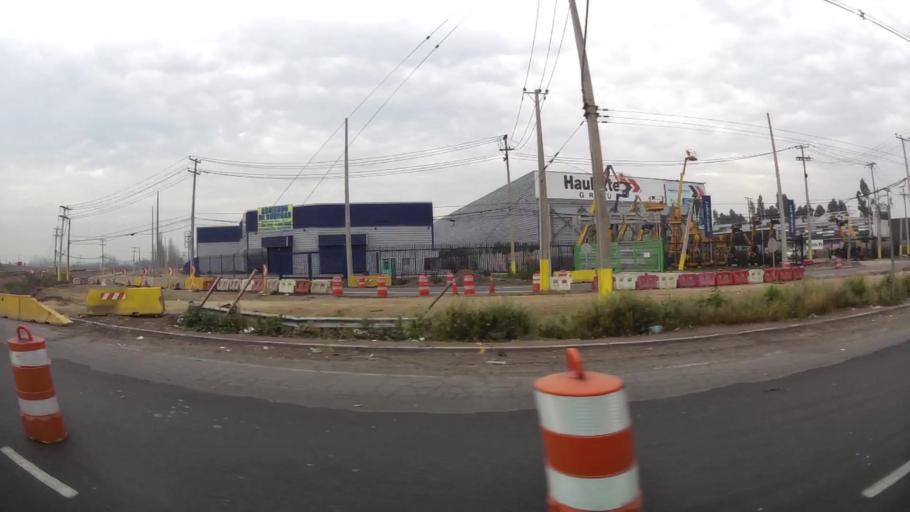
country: CL
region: Santiago Metropolitan
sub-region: Provincia de Chacabuco
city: Chicureo Abajo
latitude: -33.2749
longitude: -70.7411
